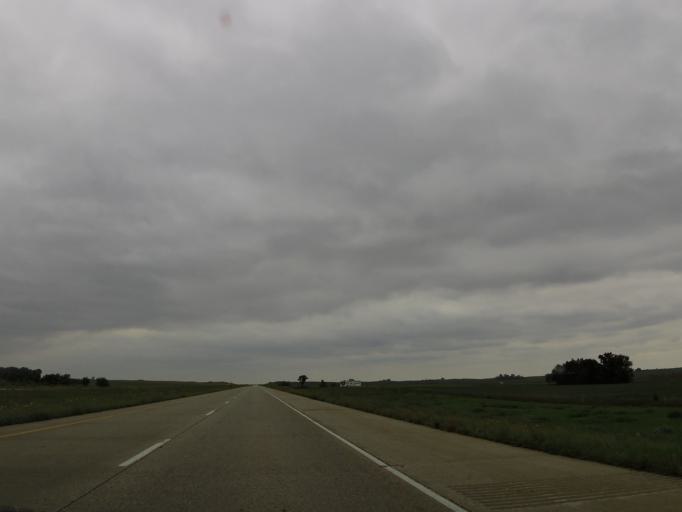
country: US
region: South Dakota
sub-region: Roberts County
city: Sisseton
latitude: 45.6214
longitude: -96.9892
